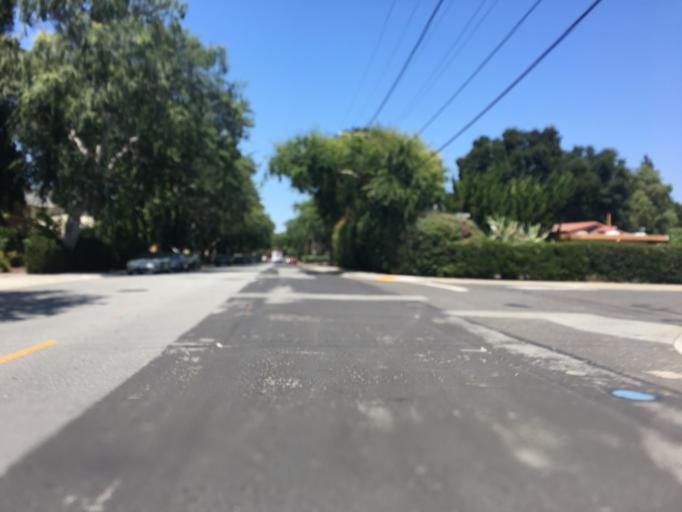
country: US
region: California
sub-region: Santa Clara County
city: Los Altos
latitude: 37.4106
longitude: -122.1194
